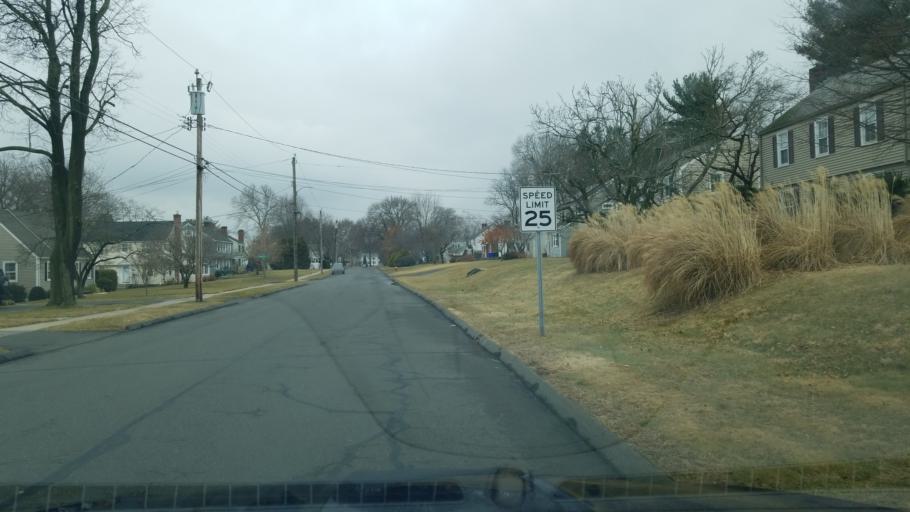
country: US
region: Connecticut
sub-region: Hartford County
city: Wethersfield
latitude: 41.7024
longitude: -72.6656
